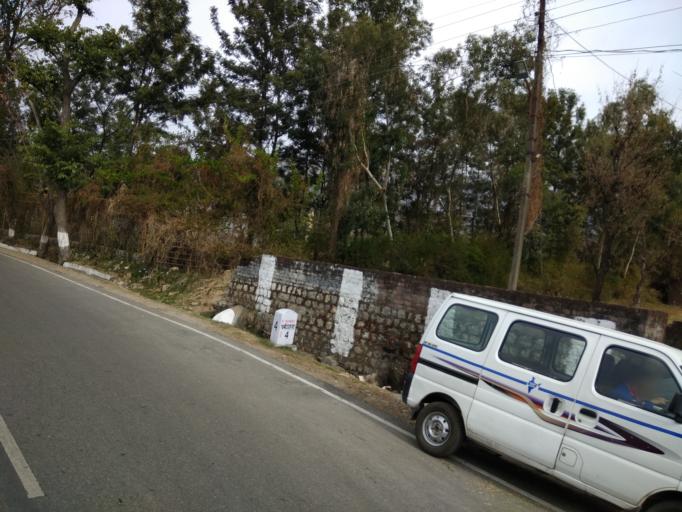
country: IN
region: Himachal Pradesh
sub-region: Kangra
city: Dharmsala
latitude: 32.1934
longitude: 76.3475
